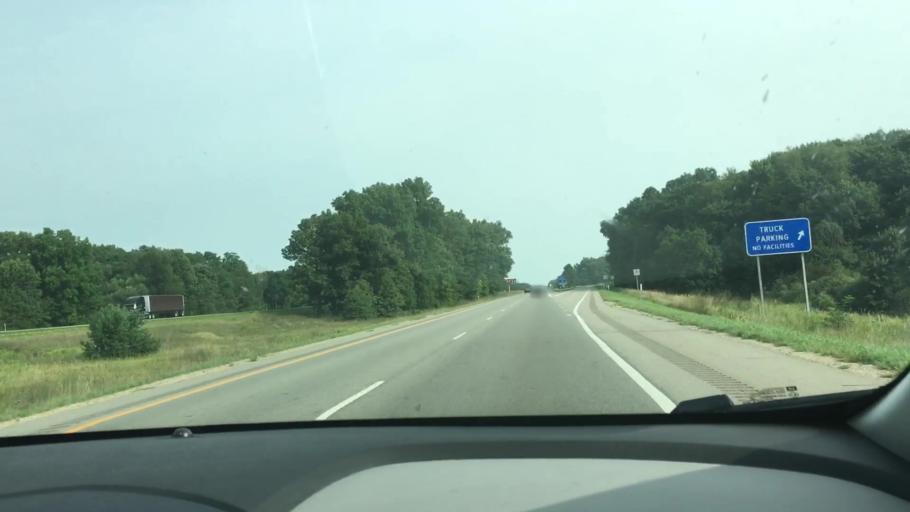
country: US
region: Michigan
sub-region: Kalamazoo County
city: Schoolcraft
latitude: 42.1678
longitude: -85.6445
